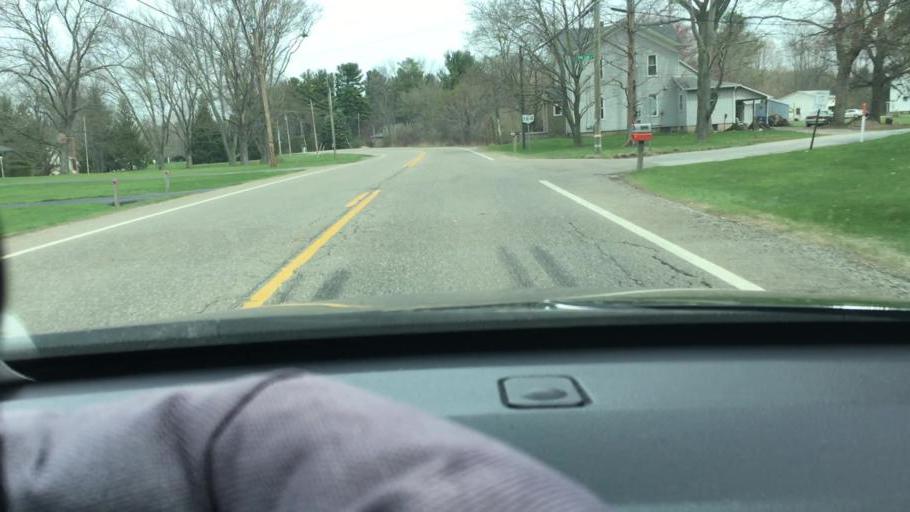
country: US
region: Ohio
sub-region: Columbiana County
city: Columbiana
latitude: 40.9293
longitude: -80.6761
